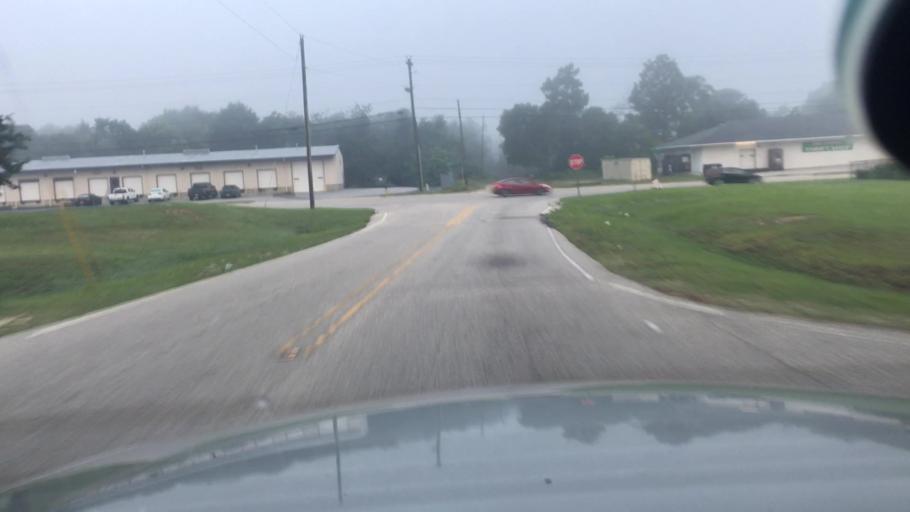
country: US
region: North Carolina
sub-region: Cumberland County
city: Hope Mills
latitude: 35.0164
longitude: -78.9178
